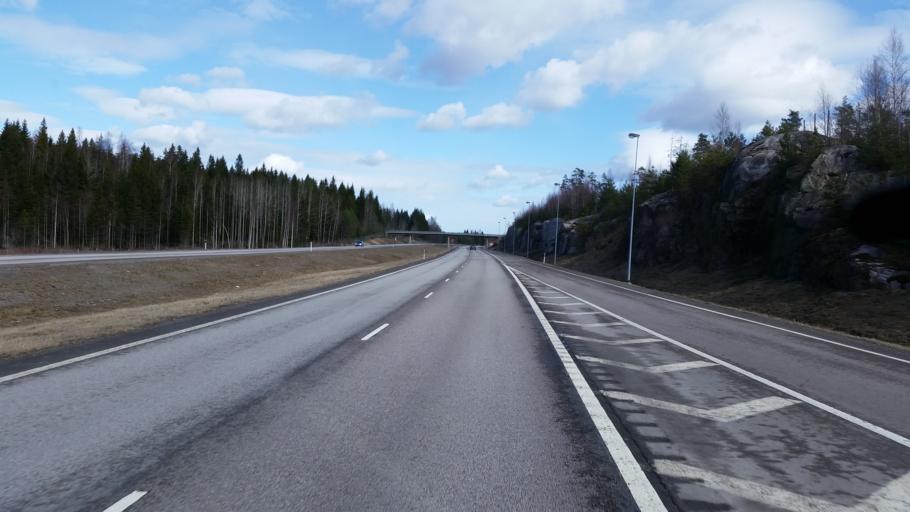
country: FI
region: Uusimaa
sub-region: Porvoo
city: Porvoo
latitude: 60.4520
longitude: 25.8388
